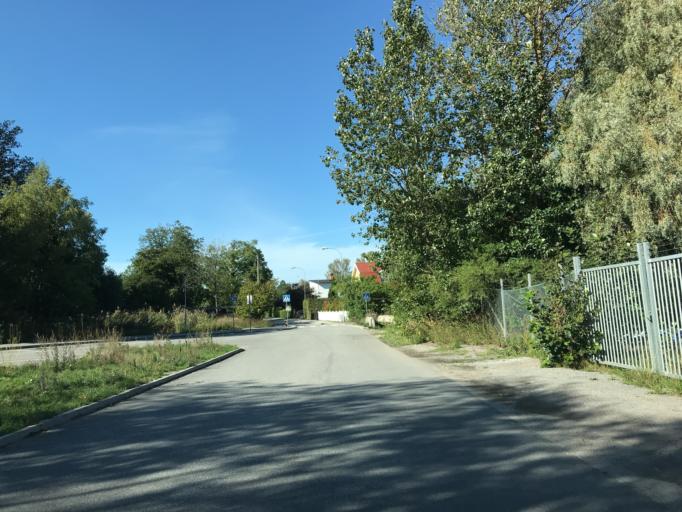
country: SE
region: Stockholm
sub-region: Sollentuna Kommun
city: Sollentuna
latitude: 59.4125
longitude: 17.9852
